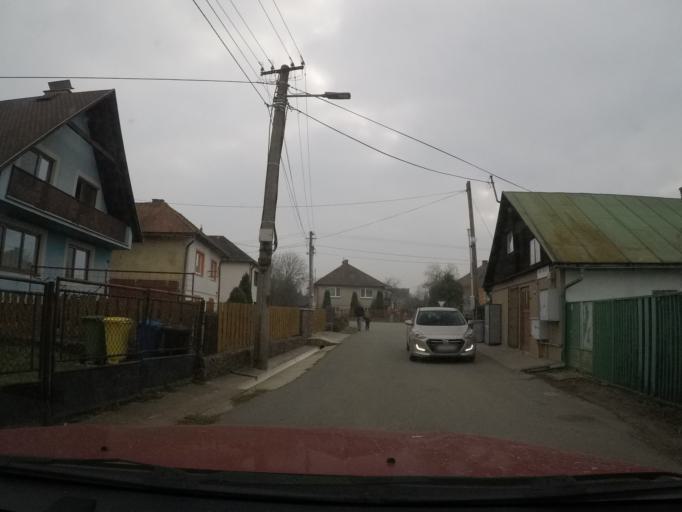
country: SK
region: Presovsky
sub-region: Okres Presov
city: Presov
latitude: 48.8731
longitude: 21.2671
